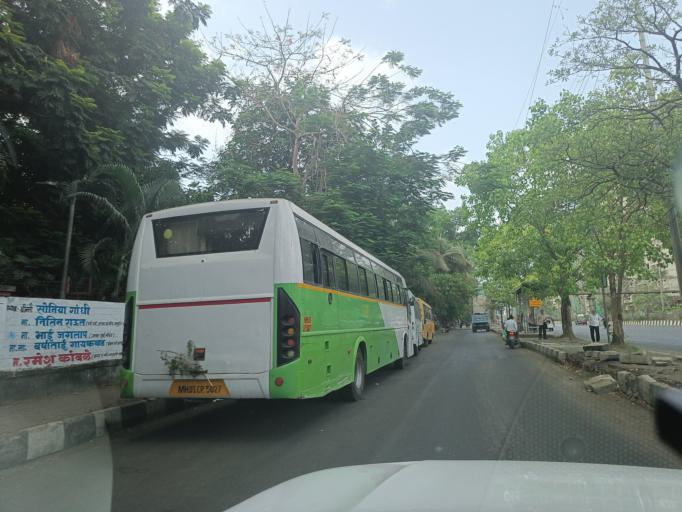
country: IN
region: Maharashtra
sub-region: Mumbai Suburban
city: Powai
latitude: 19.1169
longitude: 72.9360
